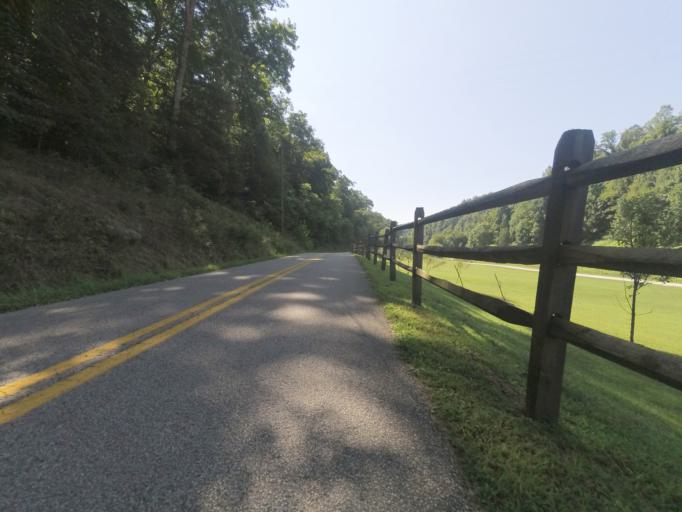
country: US
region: West Virginia
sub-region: Cabell County
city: Huntington
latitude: 38.3760
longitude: -82.4667
